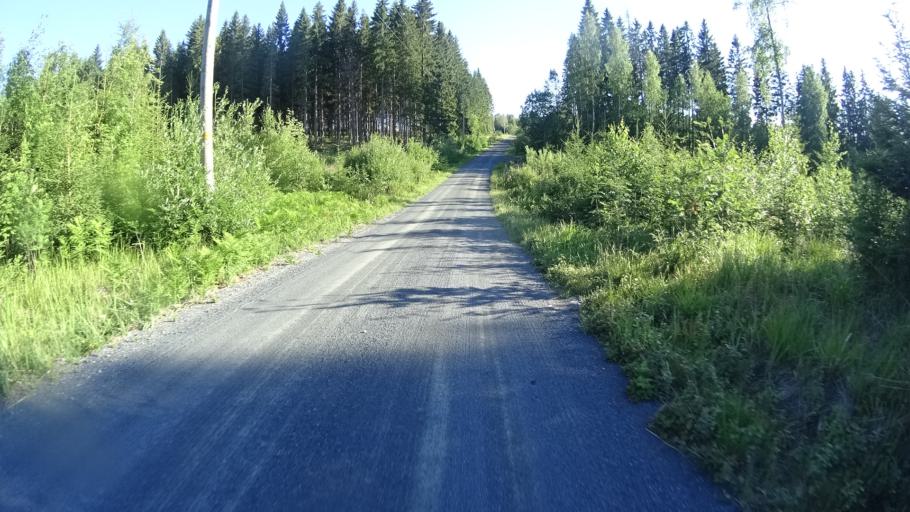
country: FI
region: Uusimaa
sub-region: Helsinki
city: Karkkila
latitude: 60.6476
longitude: 24.1256
